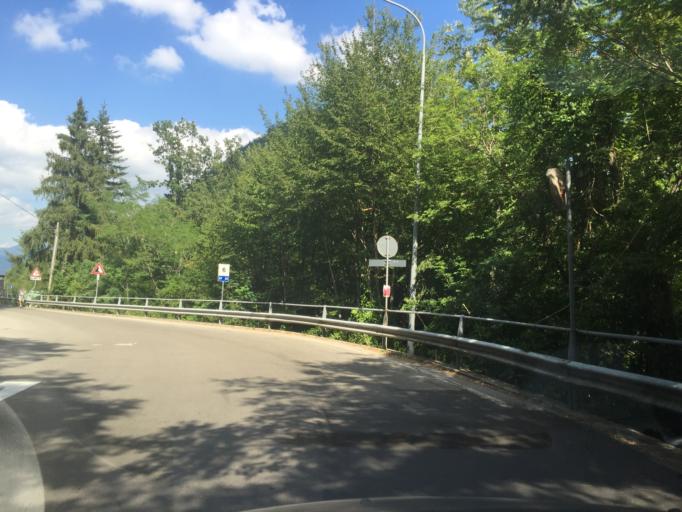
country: IT
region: Tuscany
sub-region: Provincia di Lucca
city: Careggine
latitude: 44.1266
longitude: 10.3038
